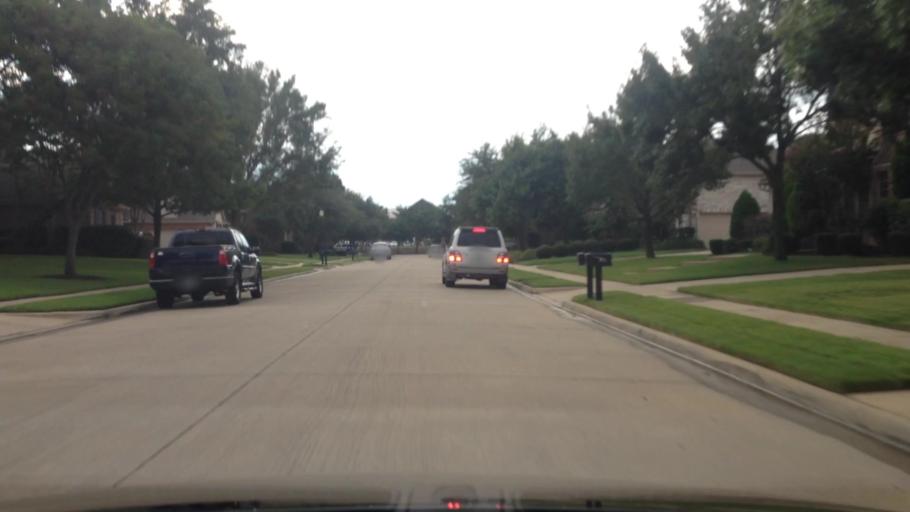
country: US
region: Texas
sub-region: Denton County
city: Flower Mound
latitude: 33.0047
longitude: -97.0442
